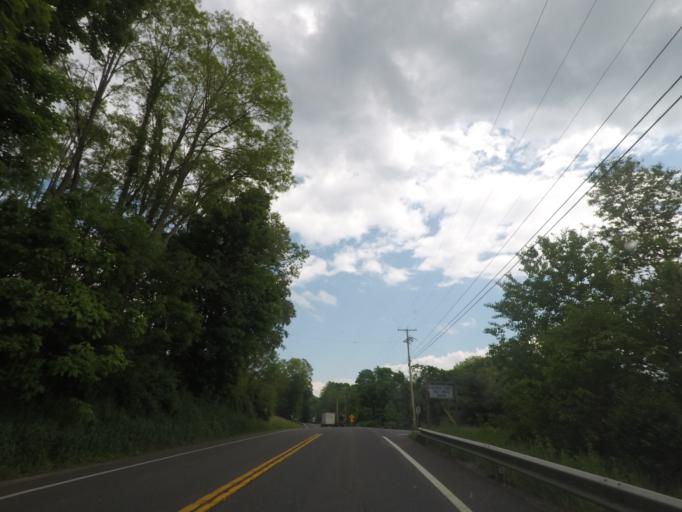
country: US
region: New York
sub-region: Dutchess County
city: Pine Plains
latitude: 42.0573
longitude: -73.6558
